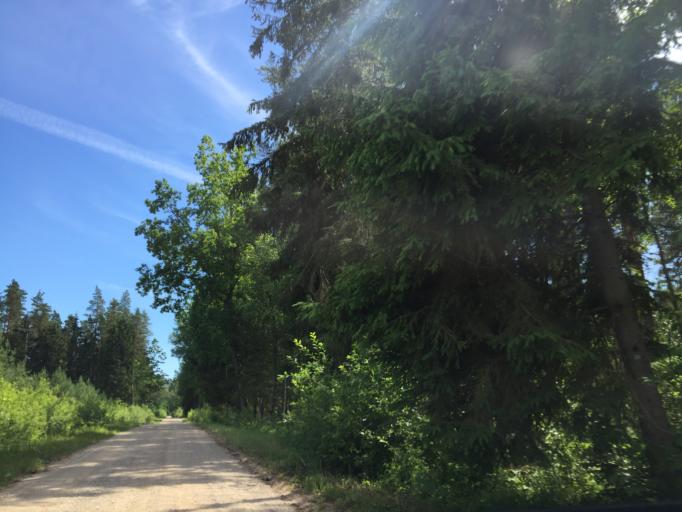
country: LV
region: Kuldigas Rajons
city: Kuldiga
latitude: 57.1219
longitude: 21.8691
